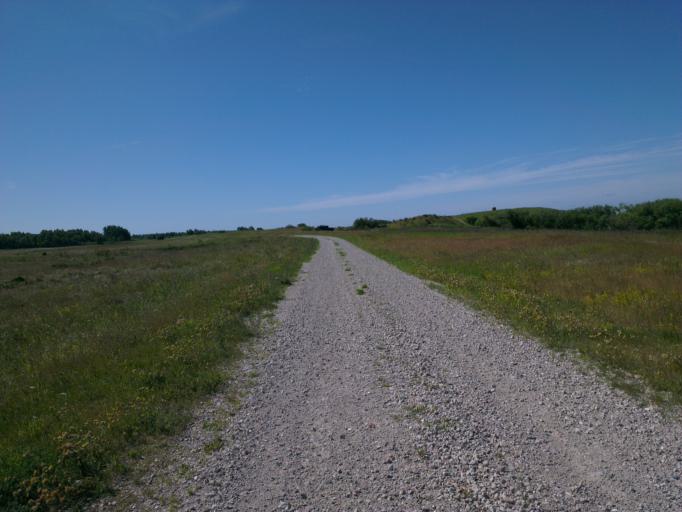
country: DK
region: Capital Region
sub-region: Frederikssund Kommune
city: Jaegerspris
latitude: 55.8890
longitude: 11.9329
